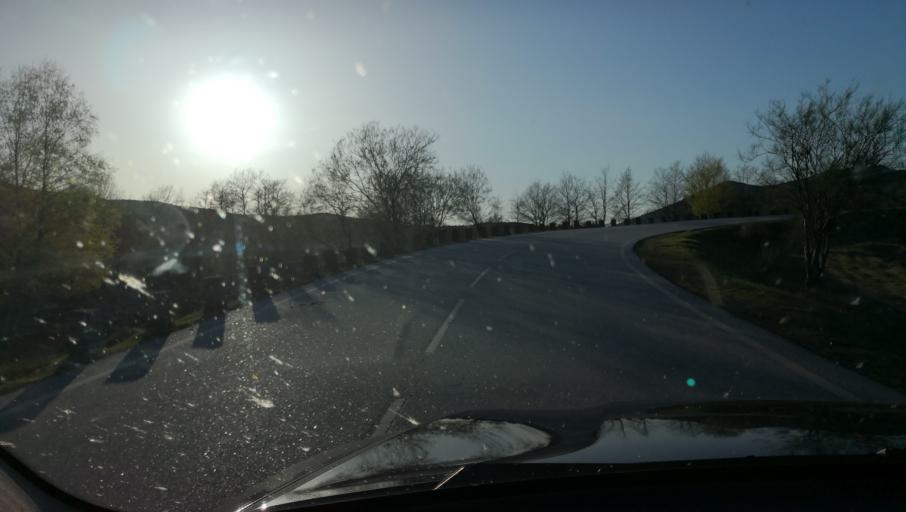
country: PT
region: Vila Real
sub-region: Vila Real
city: Vila Real
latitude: 41.3695
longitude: -7.8018
